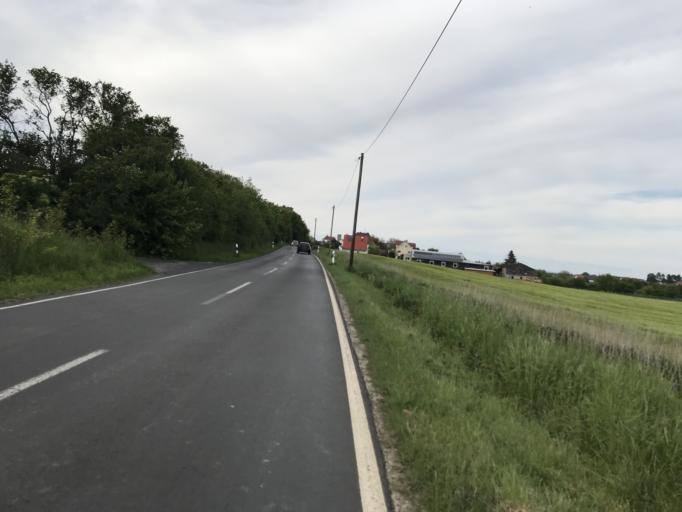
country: DE
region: Hesse
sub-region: Regierungsbezirk Giessen
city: Hoernsheim
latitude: 50.5063
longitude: 8.6140
